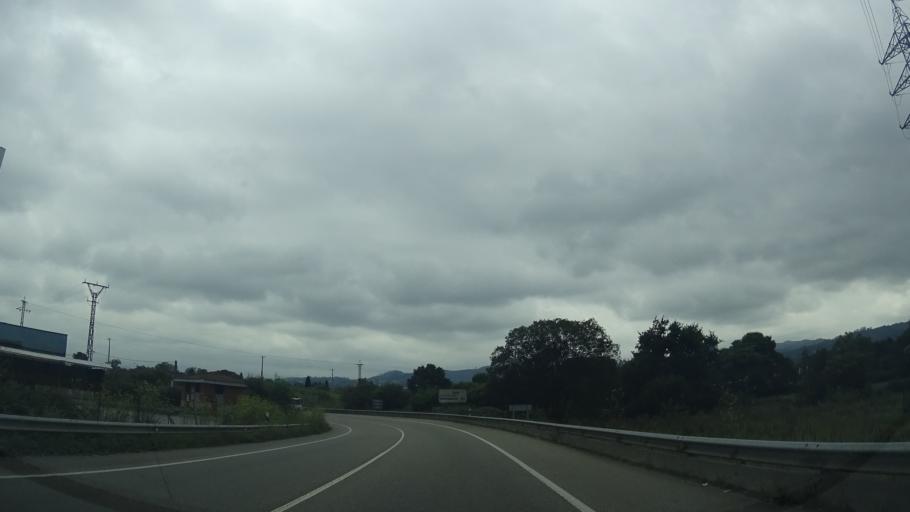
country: ES
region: Asturias
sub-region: Province of Asturias
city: Norena
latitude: 43.3821
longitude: -5.7448
